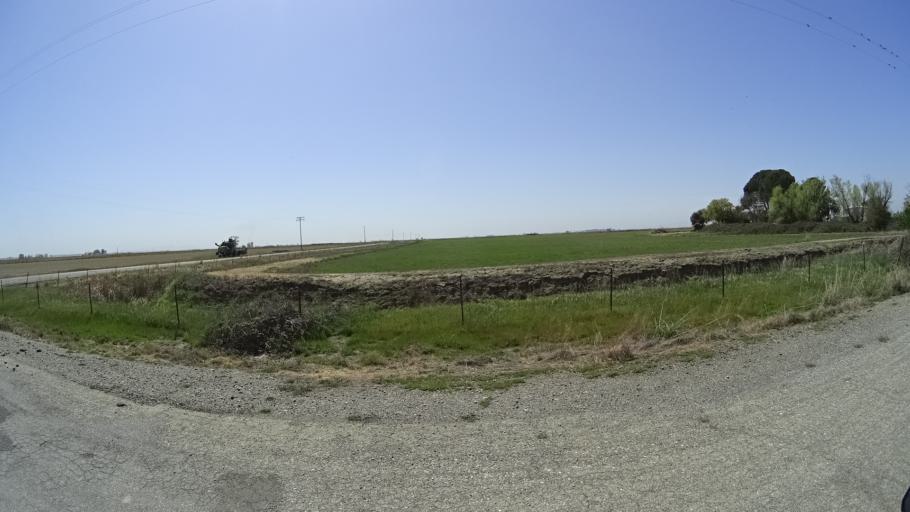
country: US
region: California
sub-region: Glenn County
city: Willows
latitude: 39.5001
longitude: -122.0939
